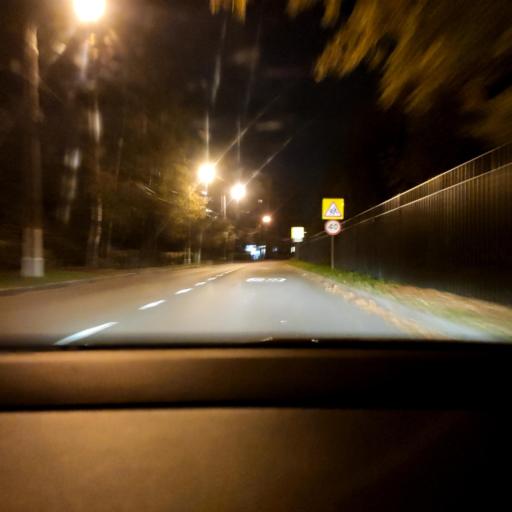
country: RU
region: Moscow
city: Khimki
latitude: 55.8957
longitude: 37.4159
